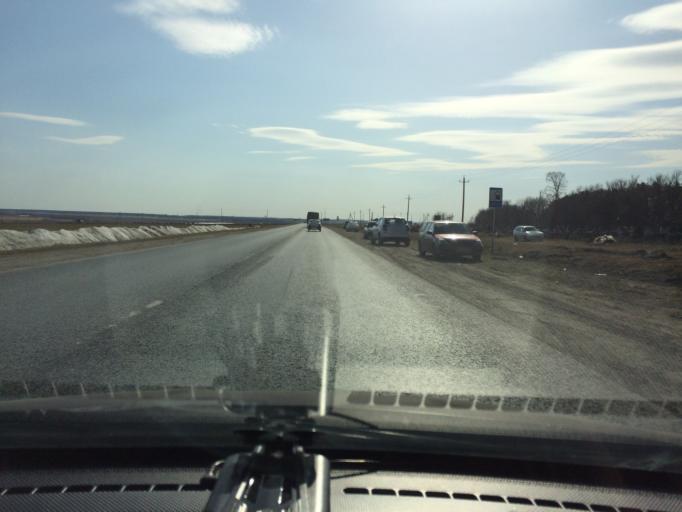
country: RU
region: Mariy-El
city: Yoshkar-Ola
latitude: 56.6995
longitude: 48.0658
